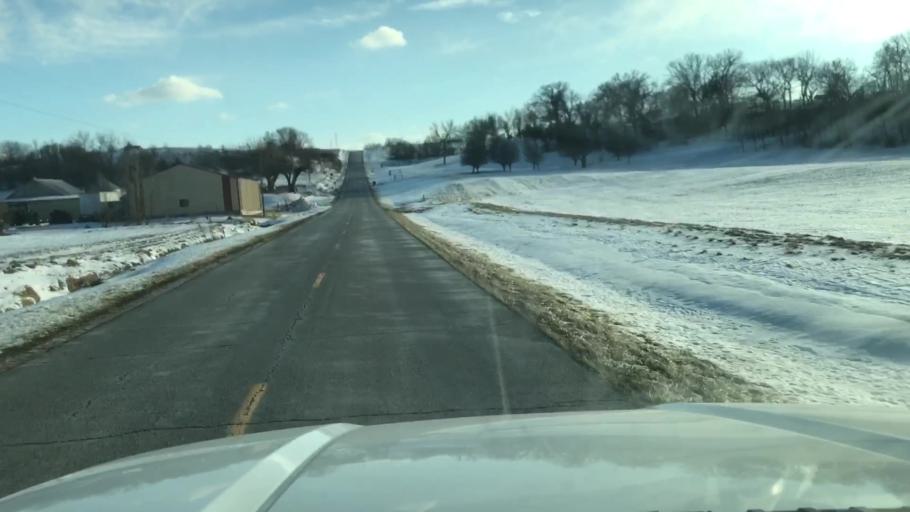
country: US
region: Missouri
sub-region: Holt County
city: Oregon
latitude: 40.0734
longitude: -94.9747
